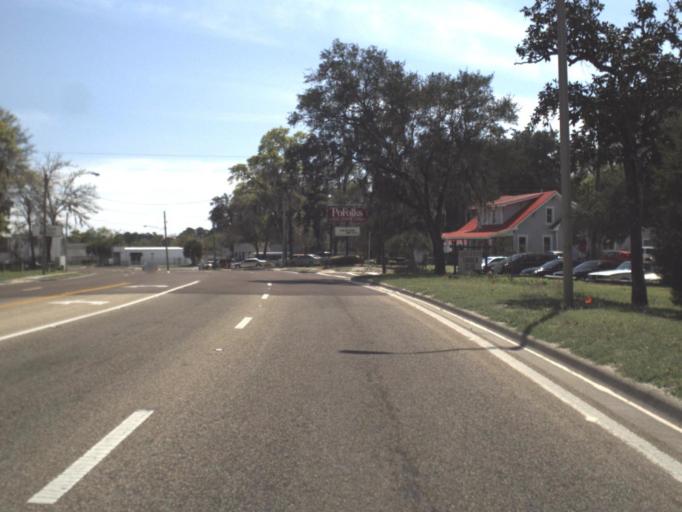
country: US
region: Florida
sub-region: Bay County
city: Lynn Haven
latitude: 30.2522
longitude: -85.6481
